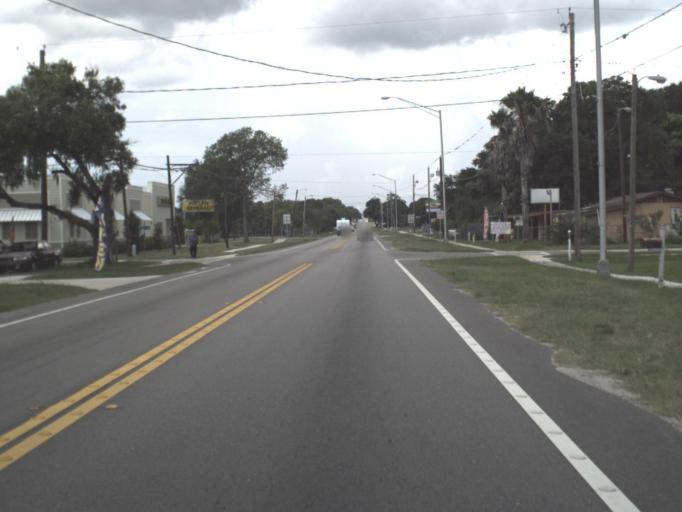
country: US
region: Florida
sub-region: Hillsborough County
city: Wimauma
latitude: 27.7125
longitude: -82.3031
